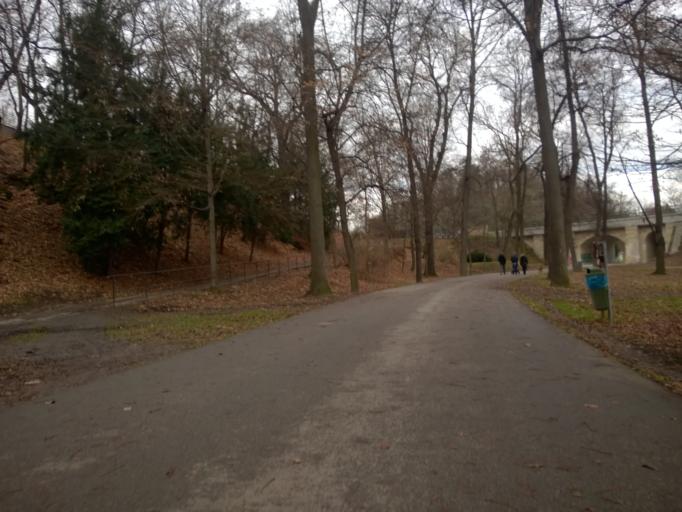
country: CZ
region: Praha
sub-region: Praha 1
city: Mala Strana
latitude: 50.1059
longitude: 14.4069
